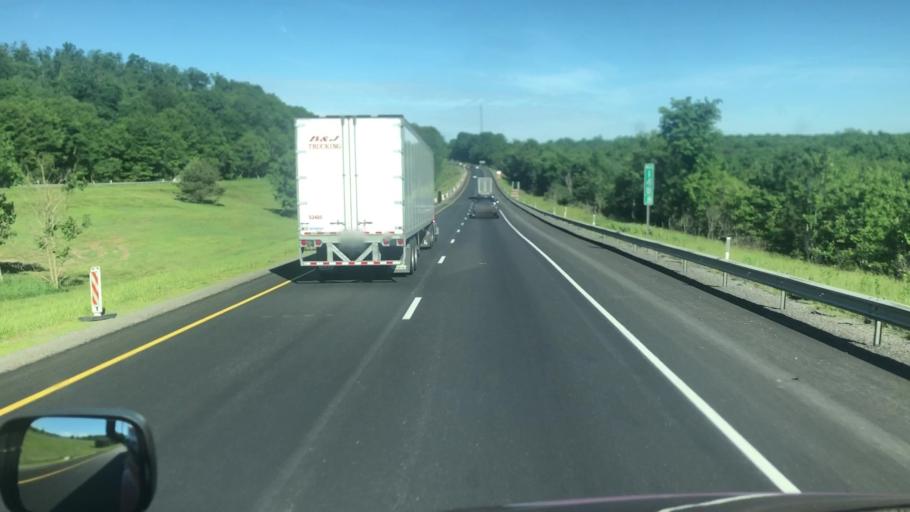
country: US
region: Pennsylvania
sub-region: Centre County
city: Milesburg
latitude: 41.0229
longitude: -77.9041
